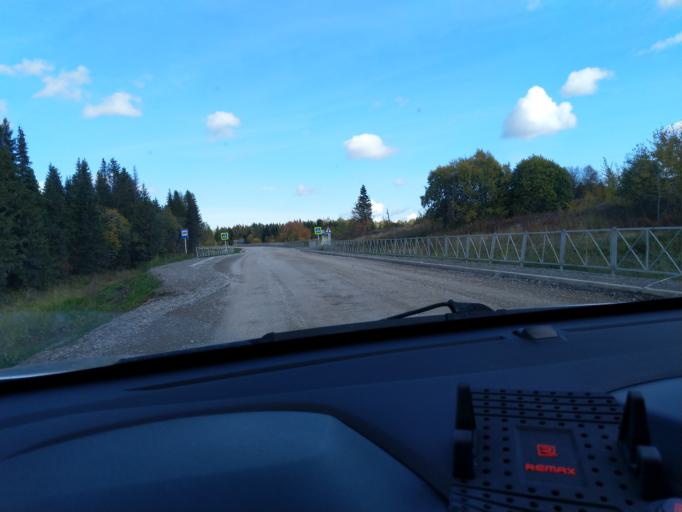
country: RU
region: Perm
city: Usol'ye
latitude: 59.4626
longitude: 56.3653
